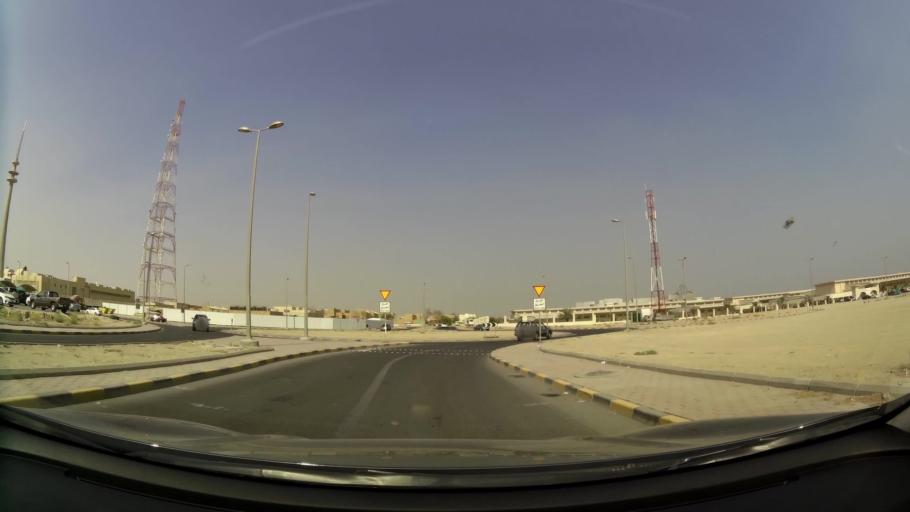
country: KW
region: Al Ahmadi
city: Al Fahahil
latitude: 29.0858
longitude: 48.1087
